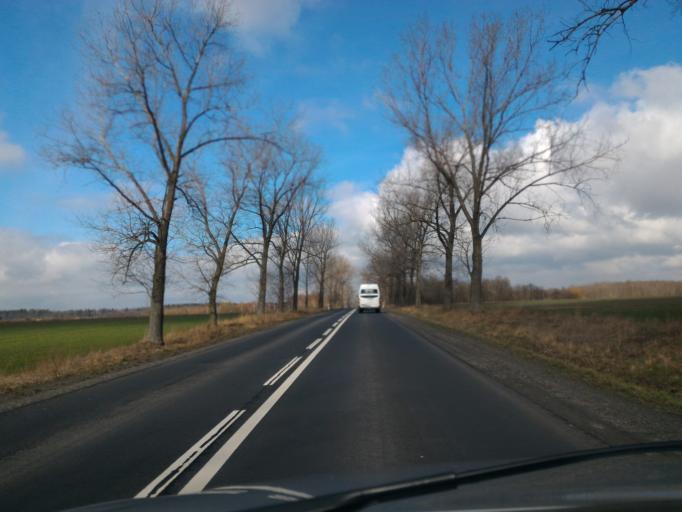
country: PL
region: Silesian Voivodeship
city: Zawidow
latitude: 51.0472
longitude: 15.0434
